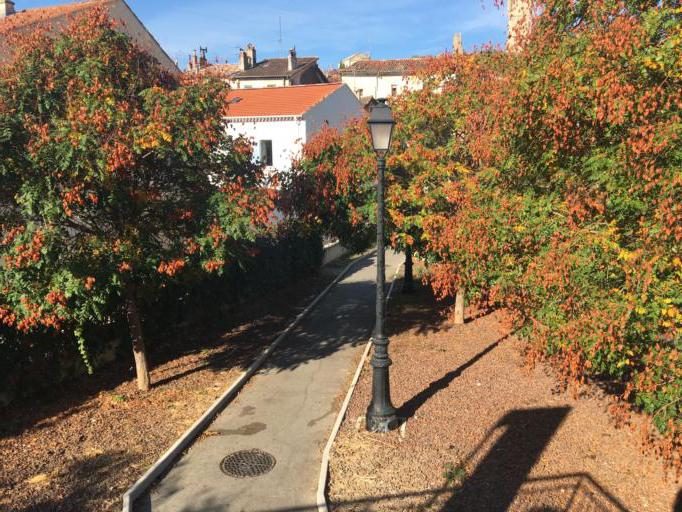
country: FR
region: Provence-Alpes-Cote d'Azur
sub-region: Departement du Var
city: Draguignan
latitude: 43.5395
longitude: 6.4685
